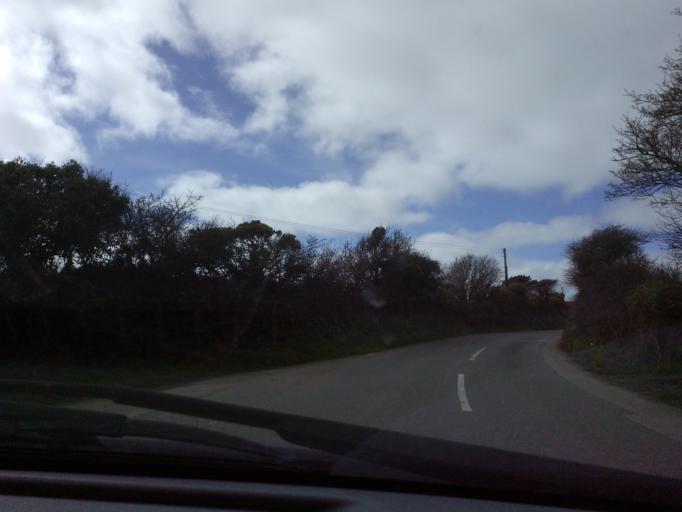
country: GB
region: England
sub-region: Cornwall
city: St. Buryan
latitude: 50.0597
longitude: -5.6340
